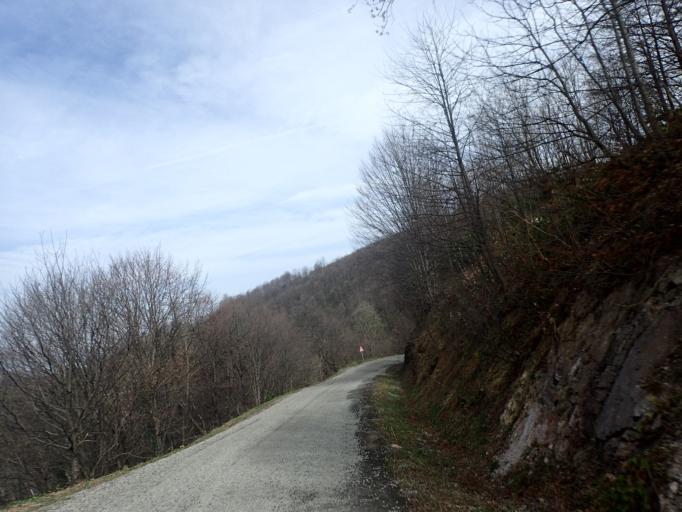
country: TR
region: Ordu
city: Kabaduz
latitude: 40.7811
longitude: 37.9186
